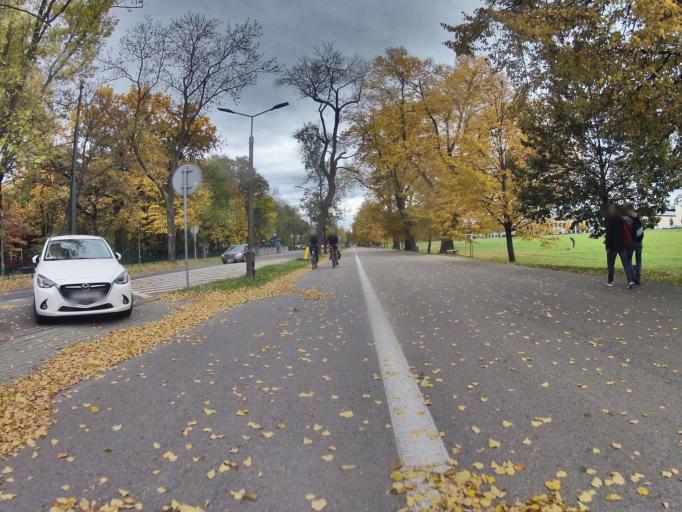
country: PL
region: Lesser Poland Voivodeship
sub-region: Krakow
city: Krakow
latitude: 50.0603
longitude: 19.9167
